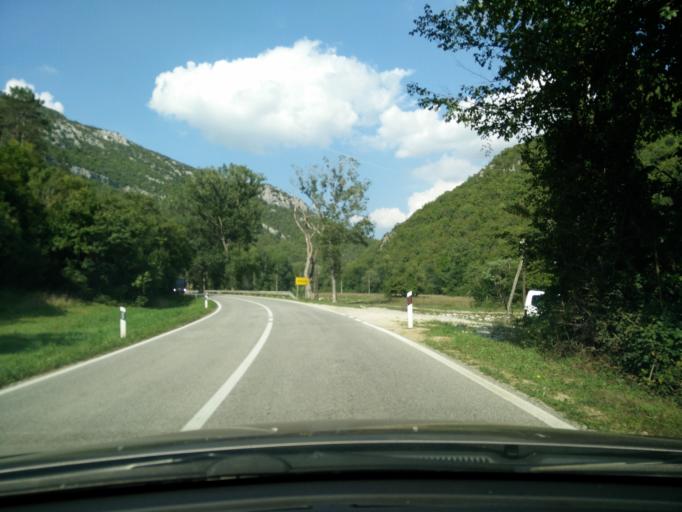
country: HR
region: Istarska
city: Buzet
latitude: 45.3865
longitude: 13.8957
